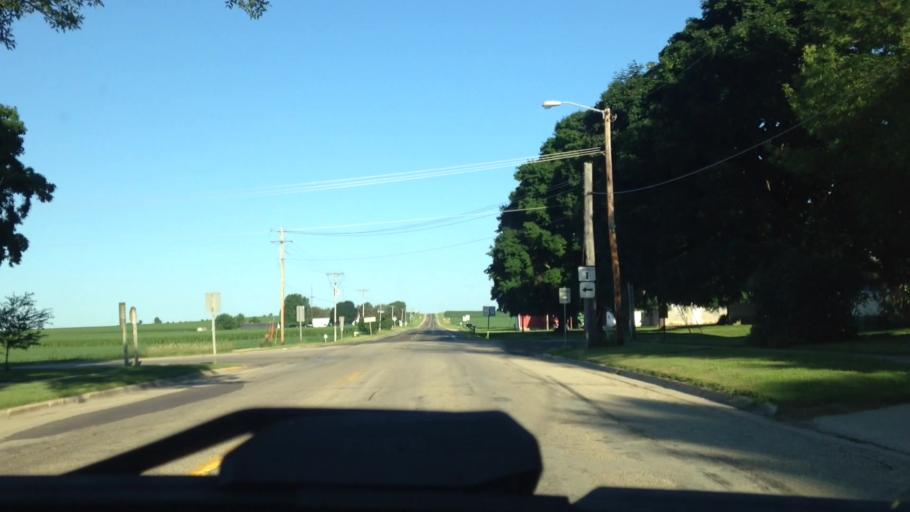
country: US
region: Wisconsin
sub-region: Columbia County
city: Poynette
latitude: 43.3377
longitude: -89.3820
